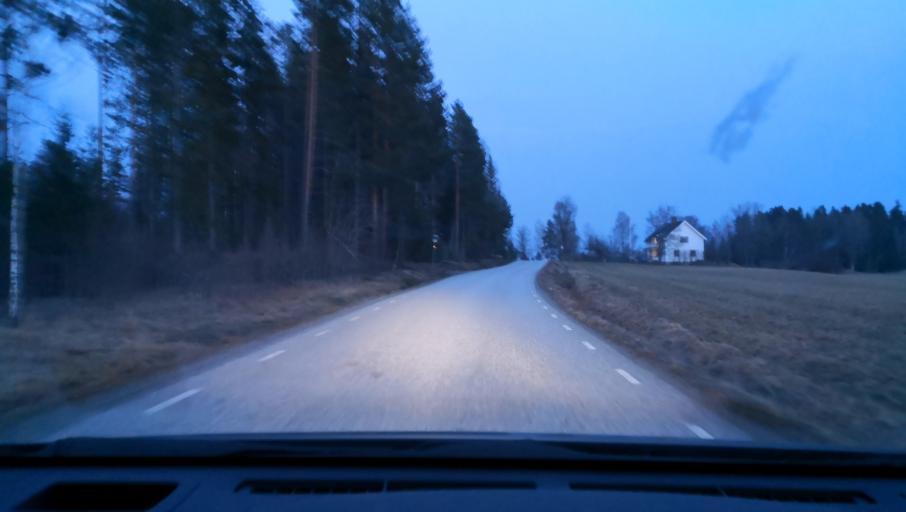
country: SE
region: OErebro
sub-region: Lindesbergs Kommun
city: Frovi
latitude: 59.5841
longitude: 15.4534
